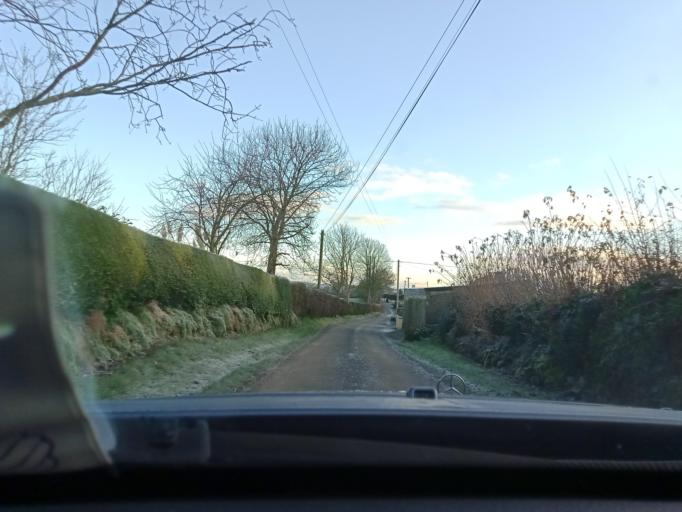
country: IE
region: Leinster
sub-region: County Carlow
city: Bagenalstown
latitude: 52.6382
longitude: -7.0161
